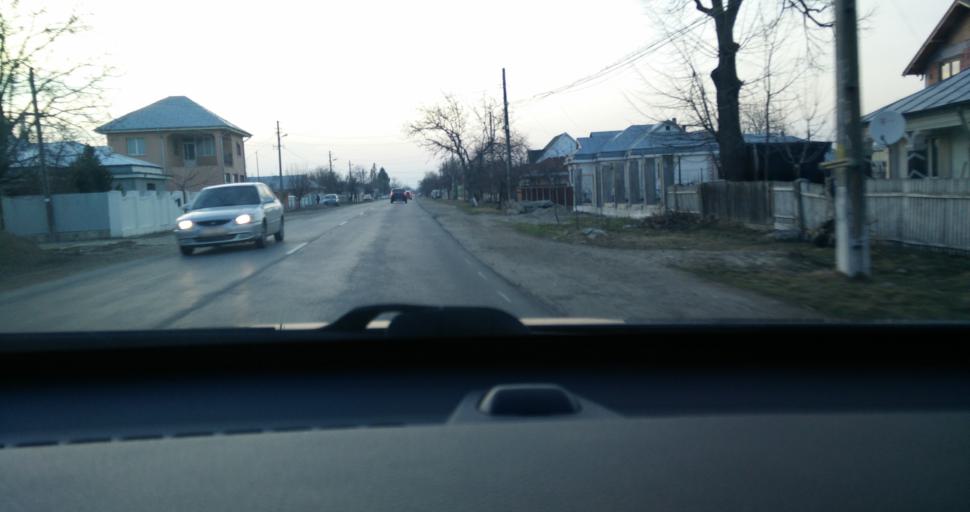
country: RO
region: Vrancea
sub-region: Comuna Rastoaca
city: Rastoaca
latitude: 45.6643
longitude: 27.2744
